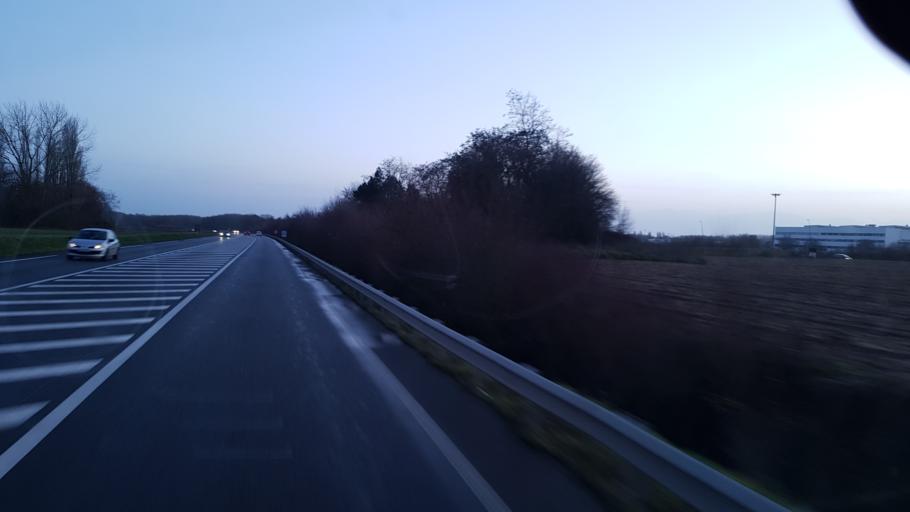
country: FR
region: Nord-Pas-de-Calais
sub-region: Departement du Nord
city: Cuincy
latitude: 50.3679
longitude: 3.0354
